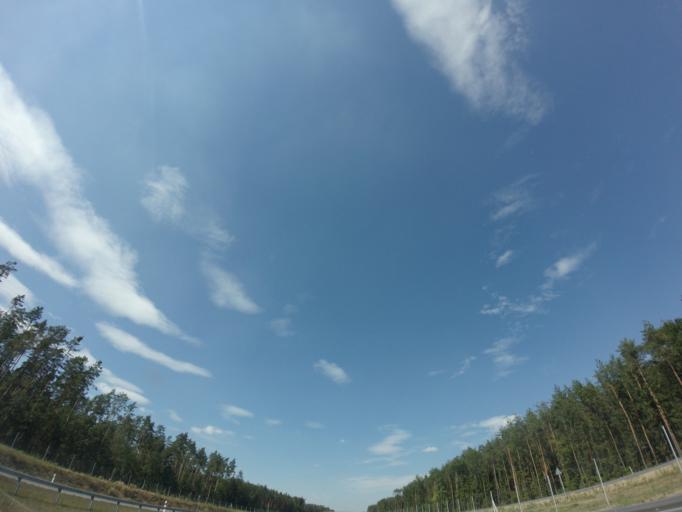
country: PL
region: Lower Silesian Voivodeship
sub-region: Powiat lubinski
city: Osiek
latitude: 51.3167
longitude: 16.1606
